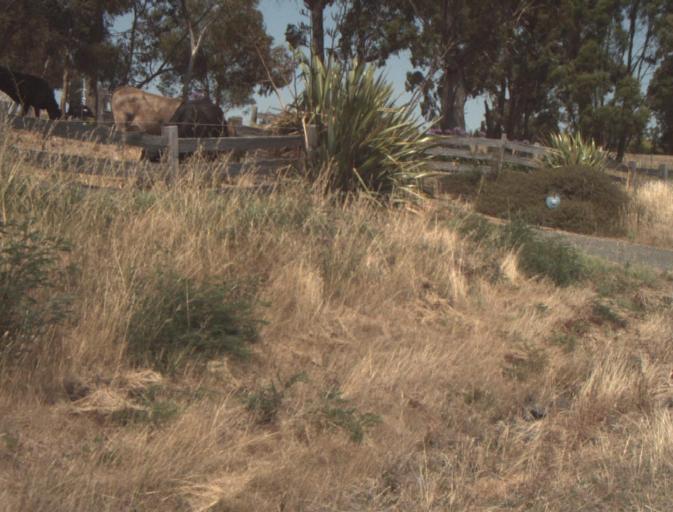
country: AU
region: Tasmania
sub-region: Launceston
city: Newstead
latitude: -41.4971
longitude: 147.2131
